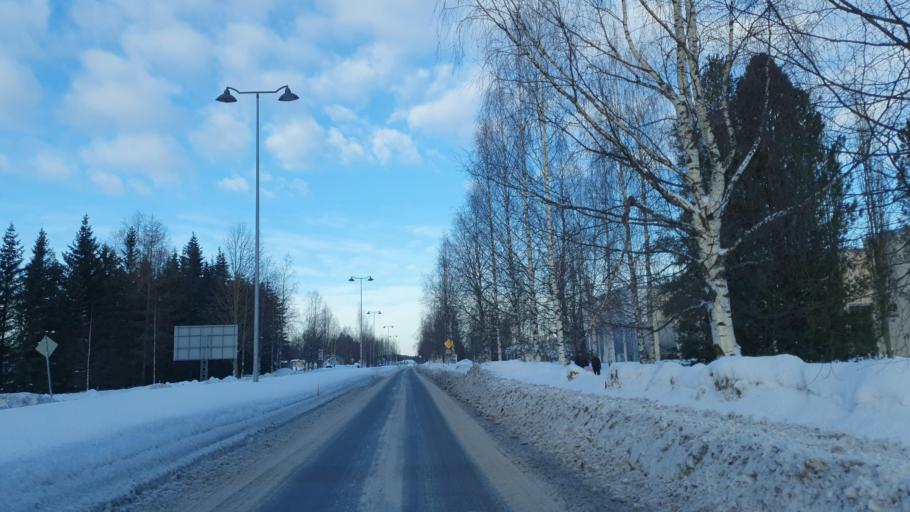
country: FI
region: Northern Ostrobothnia
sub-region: Oulu
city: Muhos
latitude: 64.8090
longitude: 25.9879
